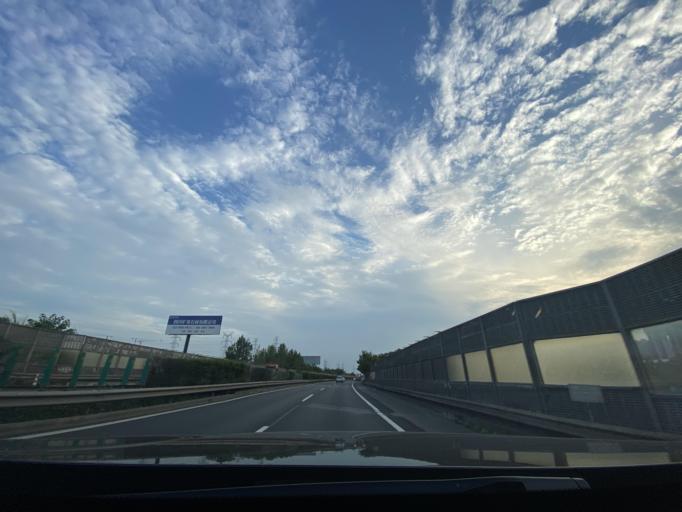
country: CN
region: Sichuan
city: Deyang
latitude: 31.0858
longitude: 104.4081
